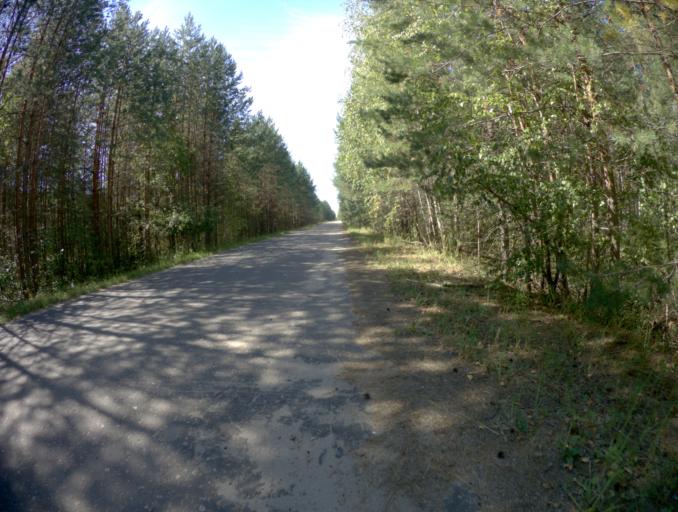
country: RU
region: Vladimir
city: Zolotkovo
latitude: 55.6005
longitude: 41.1987
